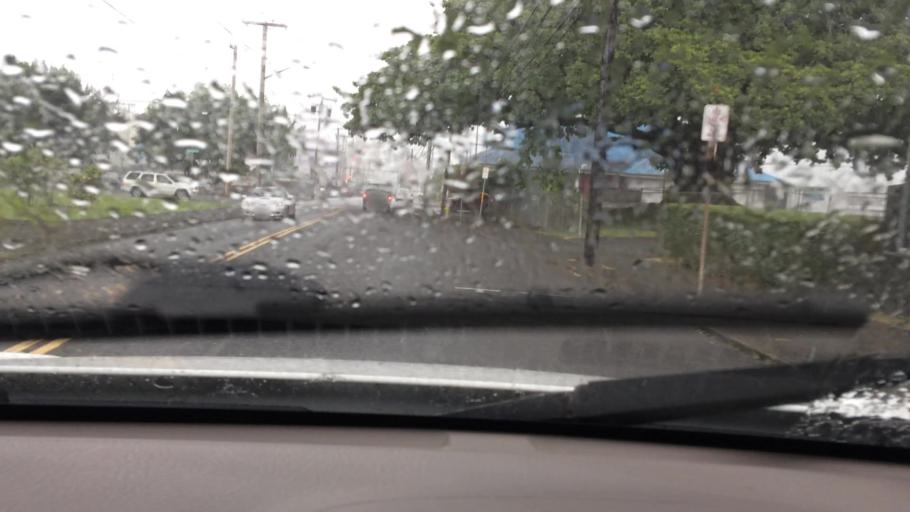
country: US
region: Hawaii
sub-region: Hawaii County
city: Hilo
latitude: 19.7227
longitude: -155.0894
